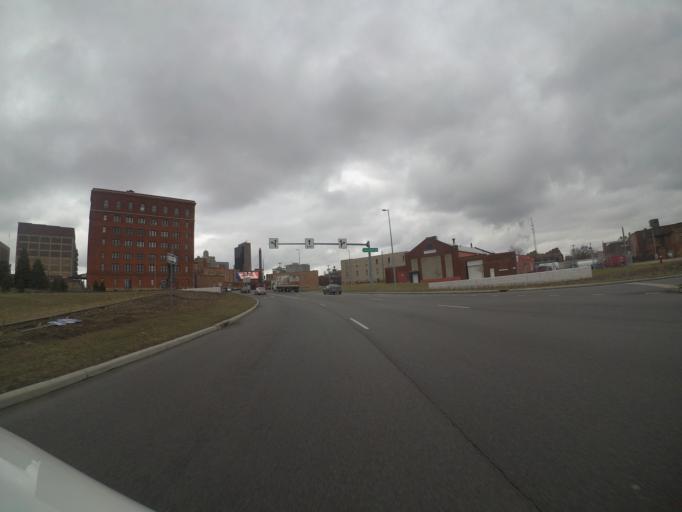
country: US
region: Ohio
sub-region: Lucas County
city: Toledo
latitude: 41.6471
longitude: -83.5435
